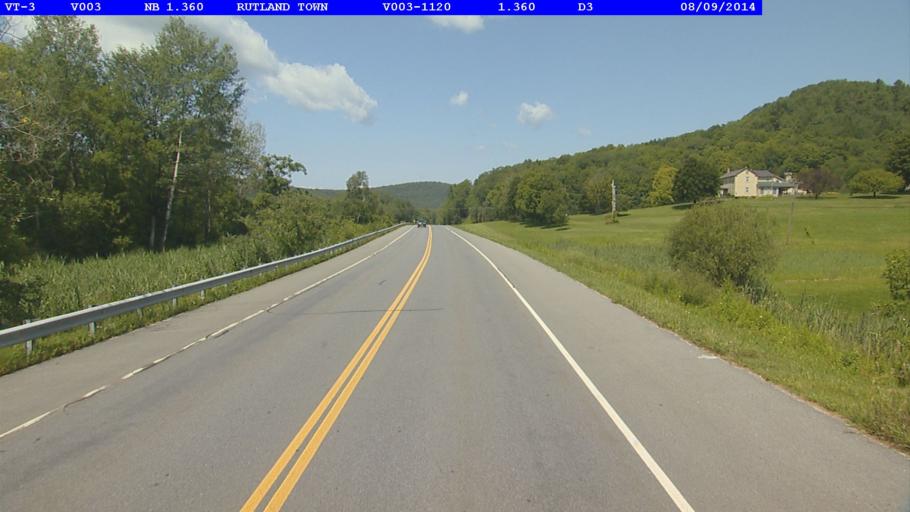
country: US
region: Vermont
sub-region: Rutland County
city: West Rutland
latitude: 43.6219
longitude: -73.0238
